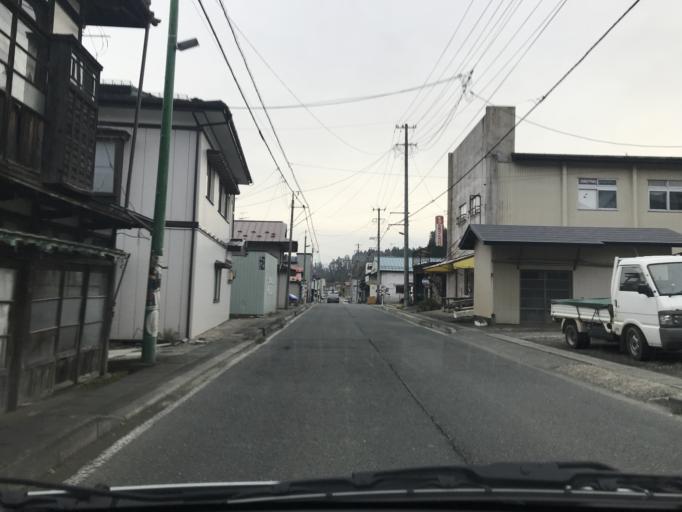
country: JP
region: Iwate
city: Kitakami
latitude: 39.2886
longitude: 141.2623
